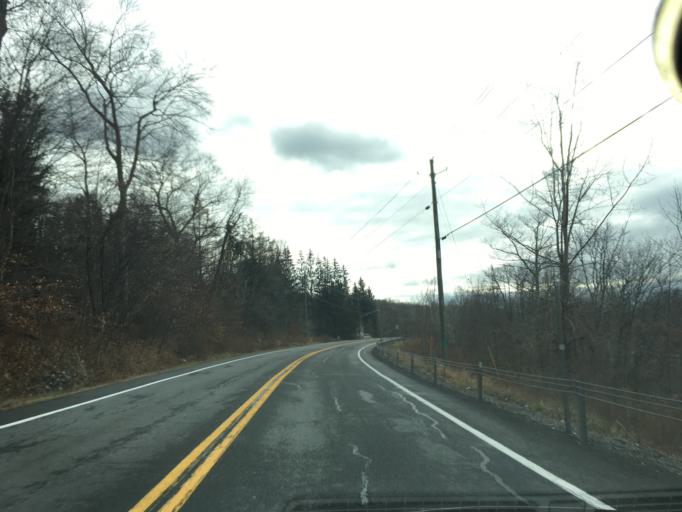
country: US
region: New York
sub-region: Rensselaer County
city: Averill Park
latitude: 42.6182
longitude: -73.5246
